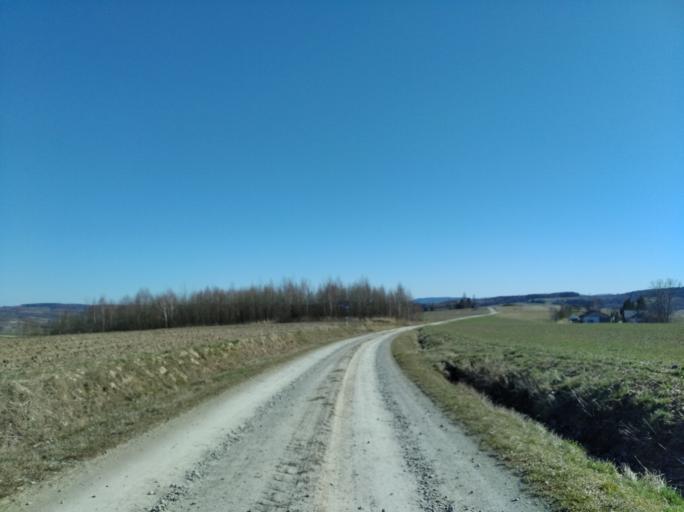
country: PL
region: Subcarpathian Voivodeship
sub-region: Powiat strzyzowski
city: Wisniowa
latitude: 49.9216
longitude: 21.6748
